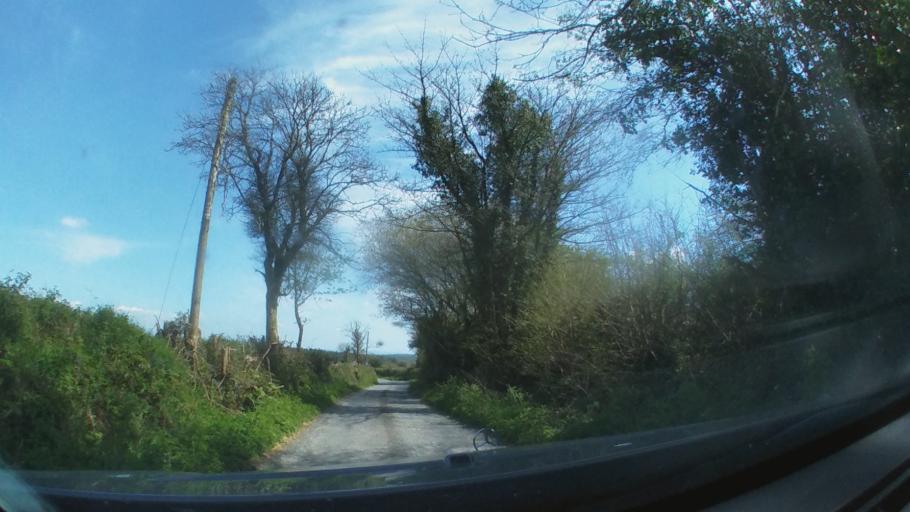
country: IE
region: Leinster
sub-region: Kilkenny
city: Callan
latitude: 52.6214
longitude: -7.5088
